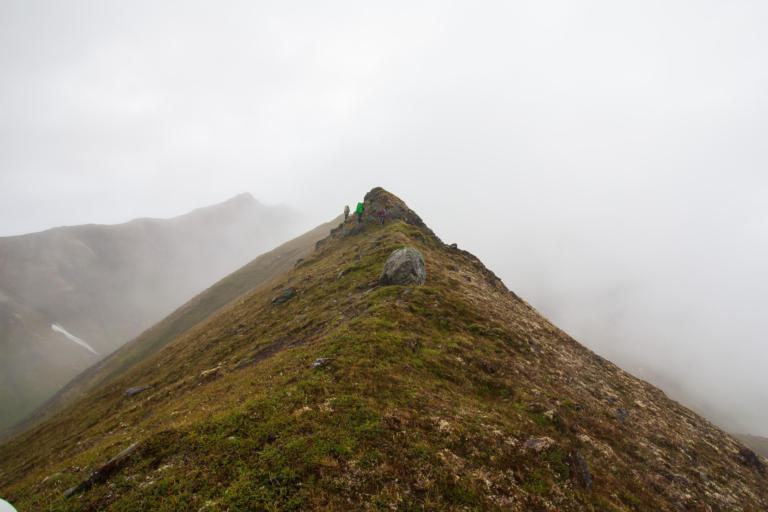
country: RU
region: Kamtsjatka
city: Yelizovo
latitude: 54.0106
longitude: 158.0852
